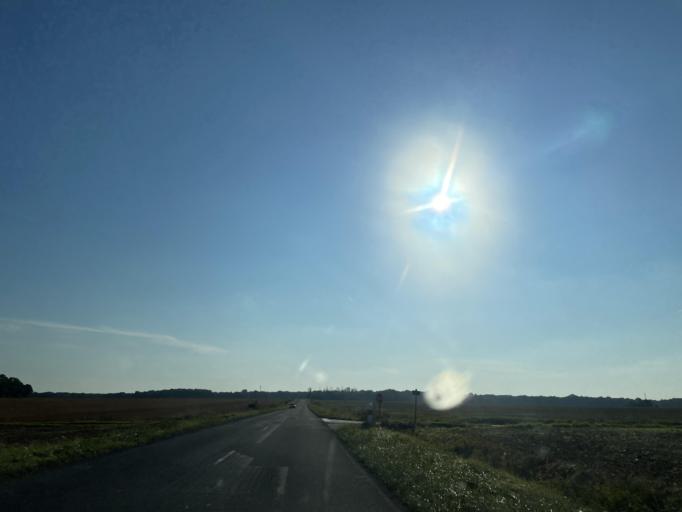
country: FR
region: Ile-de-France
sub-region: Departement de Seine-et-Marne
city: Voulangis
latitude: 48.8417
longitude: 2.8895
